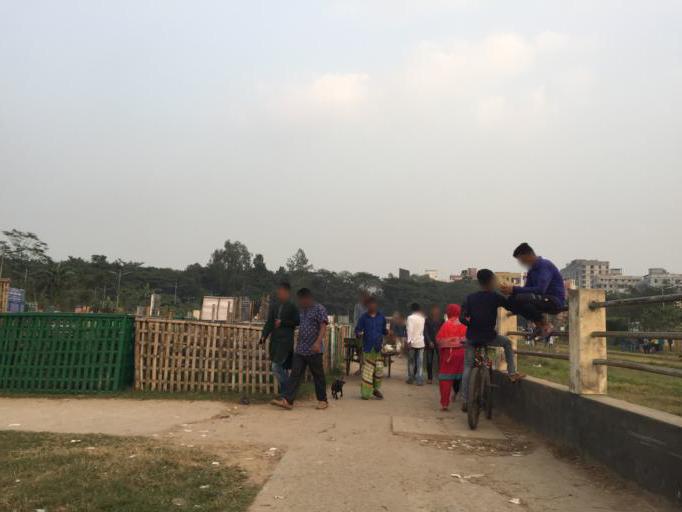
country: BD
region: Dhaka
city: Azimpur
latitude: 23.7956
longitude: 90.3447
